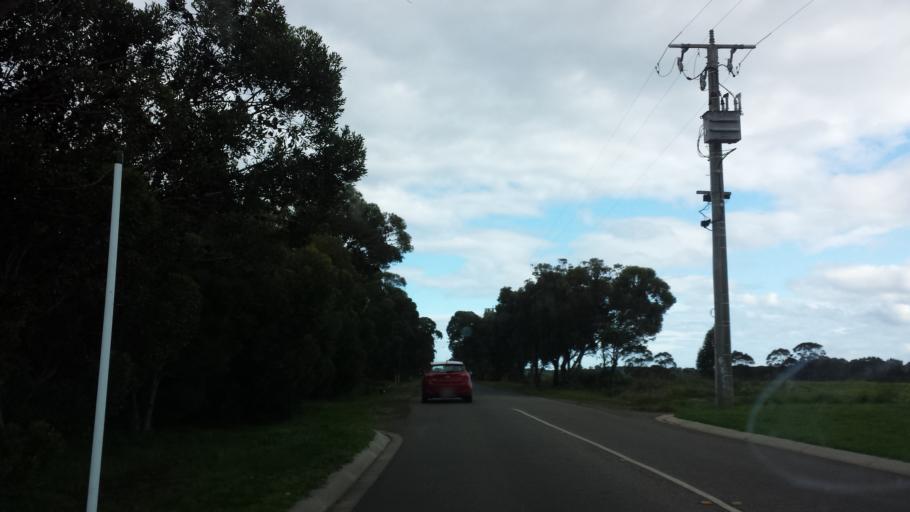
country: AU
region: Victoria
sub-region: Bass Coast
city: Cowes
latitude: -38.4604
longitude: 145.2107
